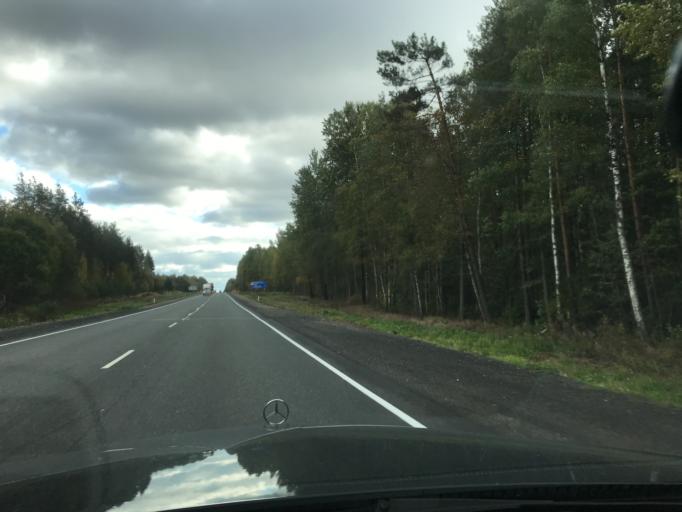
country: RU
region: Pskov
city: Opochka
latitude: 56.9678
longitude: 28.6323
